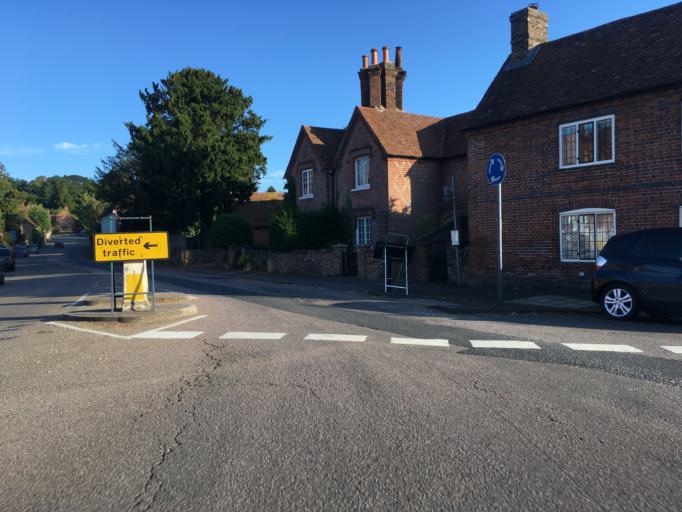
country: GB
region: England
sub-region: Hampshire
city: Tadley
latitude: 51.3838
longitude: -1.1533
